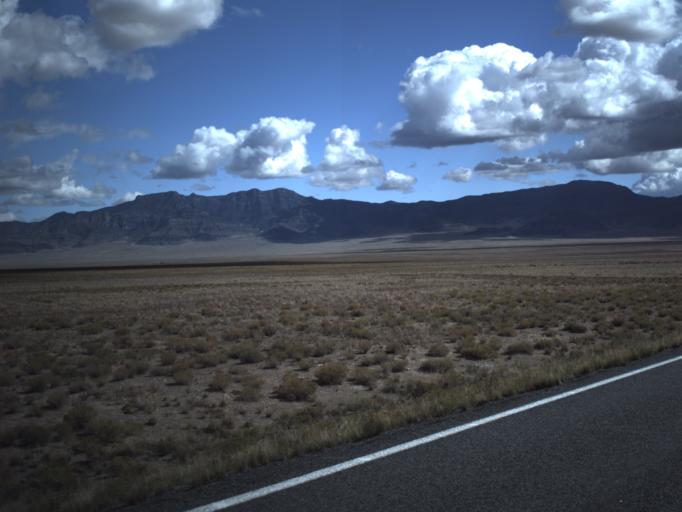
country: US
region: Utah
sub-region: Beaver County
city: Milford
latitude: 38.5556
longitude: -113.7450
